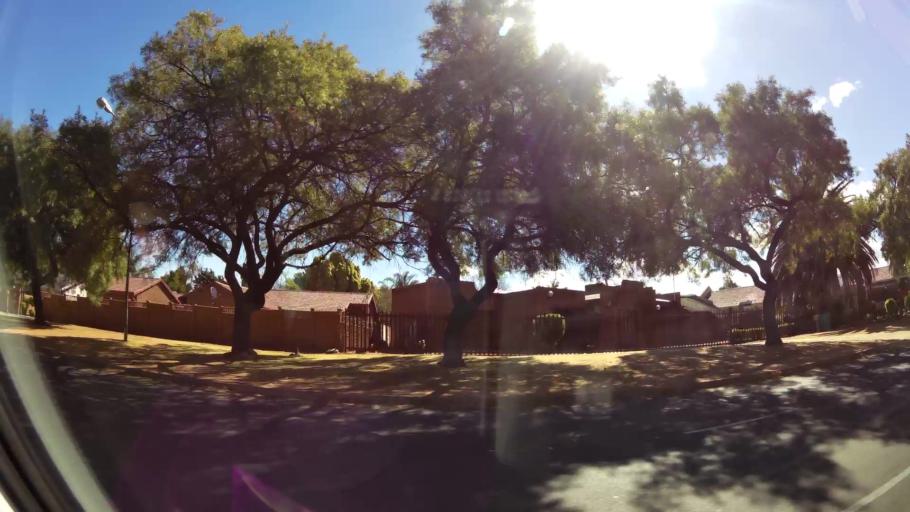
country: ZA
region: Limpopo
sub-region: Capricorn District Municipality
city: Polokwane
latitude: -23.9092
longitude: 29.4877
